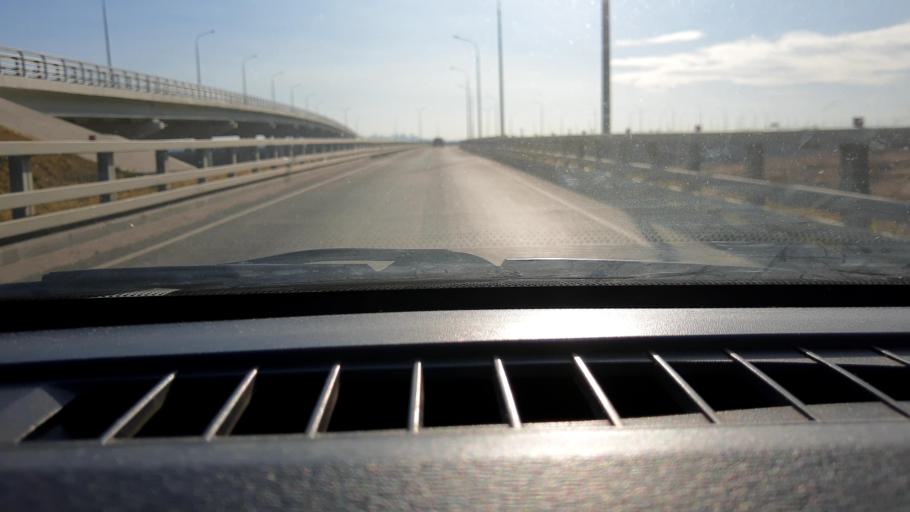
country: RU
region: Nizjnij Novgorod
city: Neklyudovo
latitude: 56.3989
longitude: 43.9904
